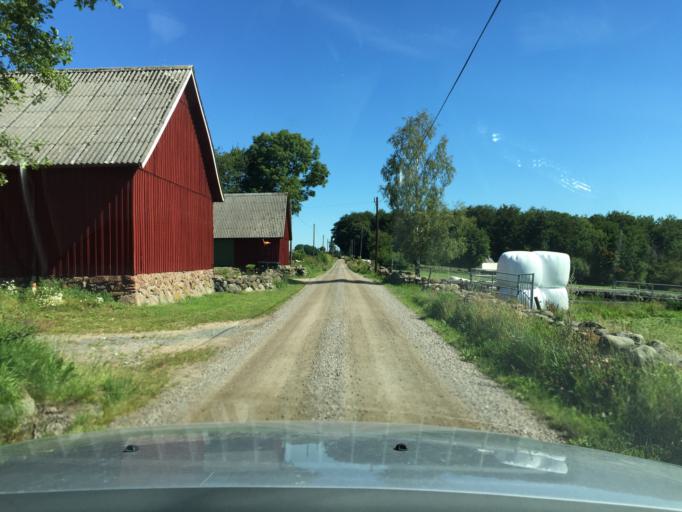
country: SE
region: Skane
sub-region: Hassleholms Kommun
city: Sosdala
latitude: 56.0157
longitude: 13.6360
